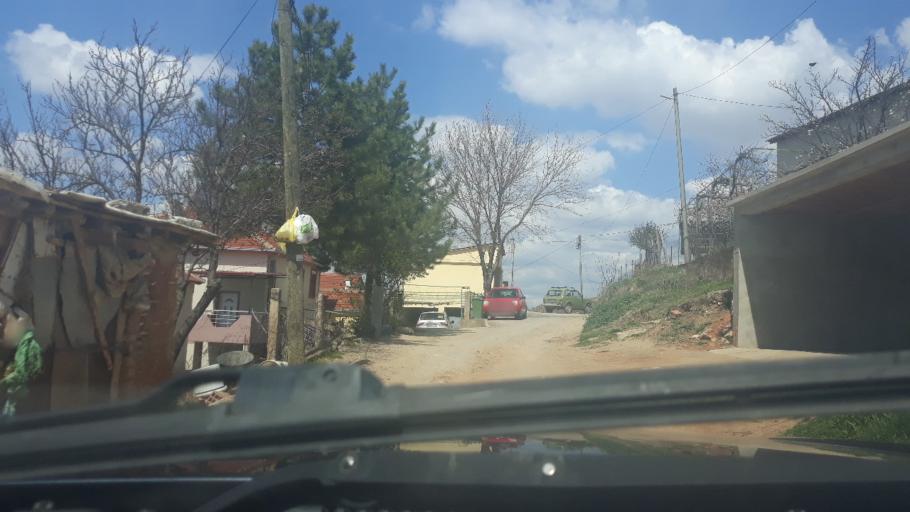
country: MK
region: Caska
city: Caska
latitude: 41.6513
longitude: 21.6937
